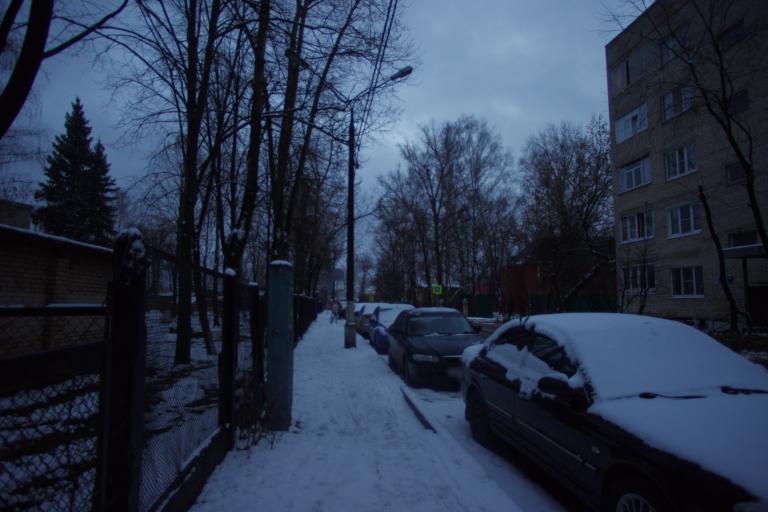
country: RU
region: Moskovskaya
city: Krasnogorsk
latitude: 55.8116
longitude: 37.3374
